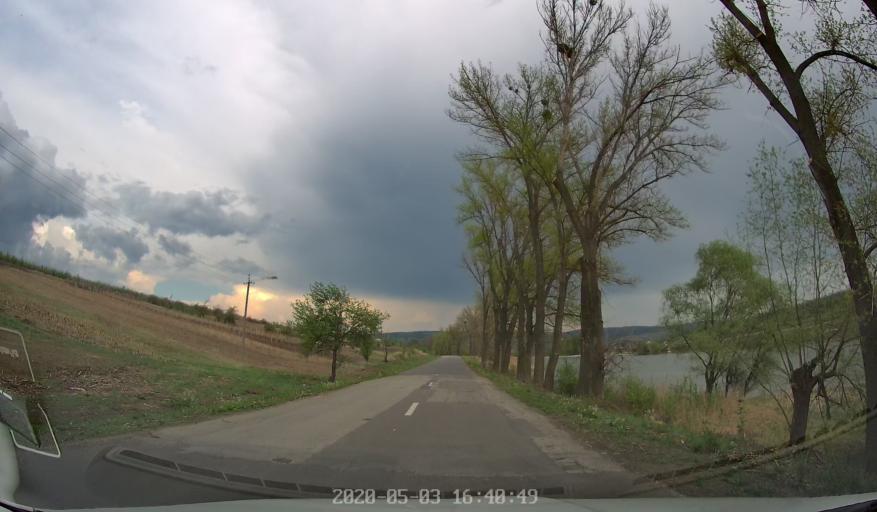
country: MD
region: Stinga Nistrului
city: Bucovat
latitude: 47.1717
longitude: 28.3983
